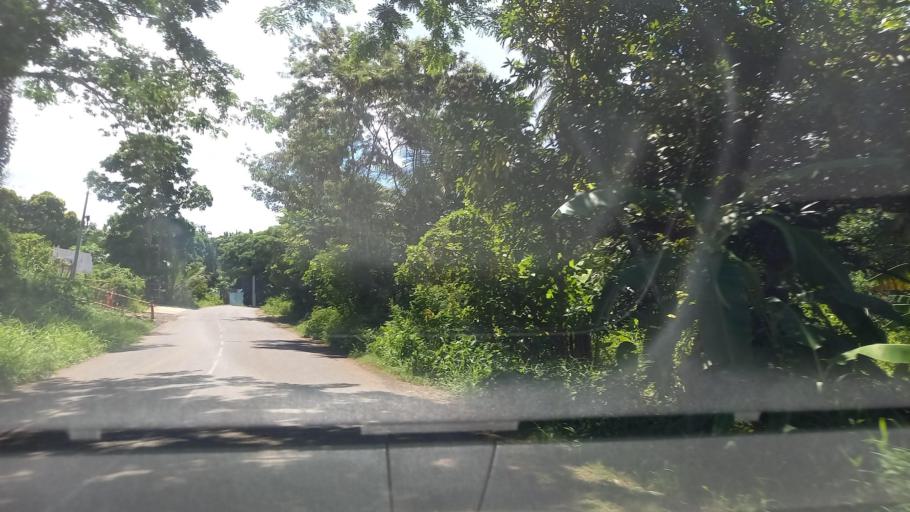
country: YT
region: Sada
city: Sada
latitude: -12.8685
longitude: 45.1155
